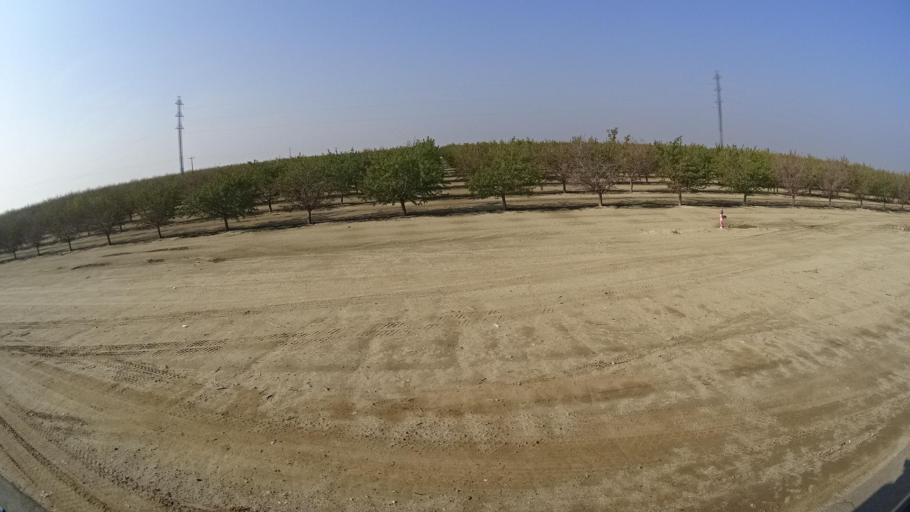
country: US
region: California
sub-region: Kern County
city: Buttonwillow
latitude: 35.4286
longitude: -119.4471
